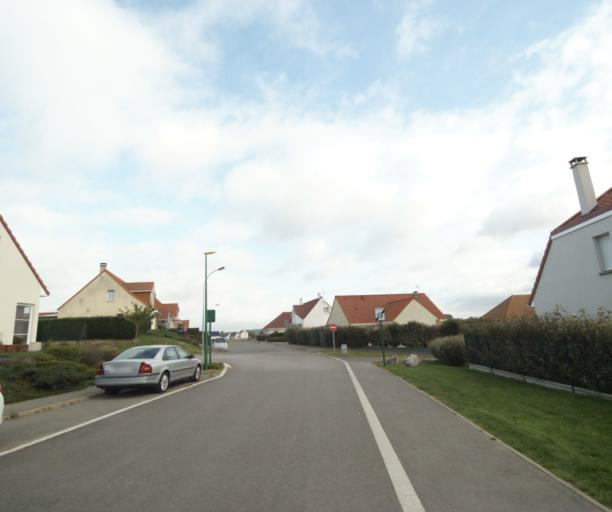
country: FR
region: Nord-Pas-de-Calais
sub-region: Departement du Pas-de-Calais
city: Etaples
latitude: 50.5143
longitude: 1.6566
